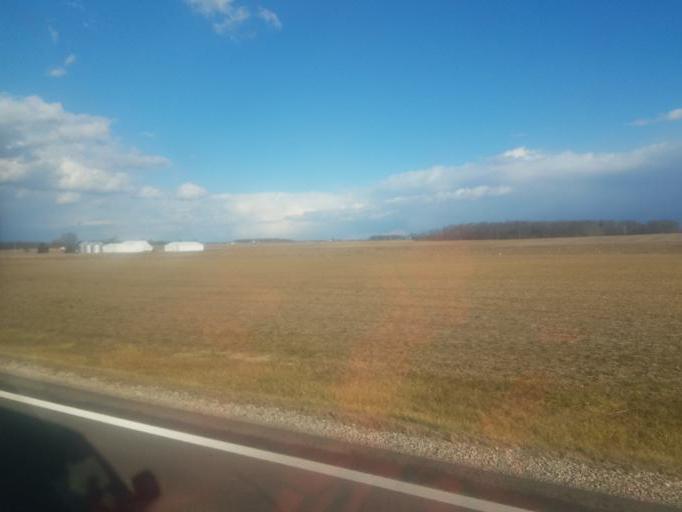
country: US
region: Ohio
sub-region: Marion County
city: Prospect
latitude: 40.3632
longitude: -83.1476
